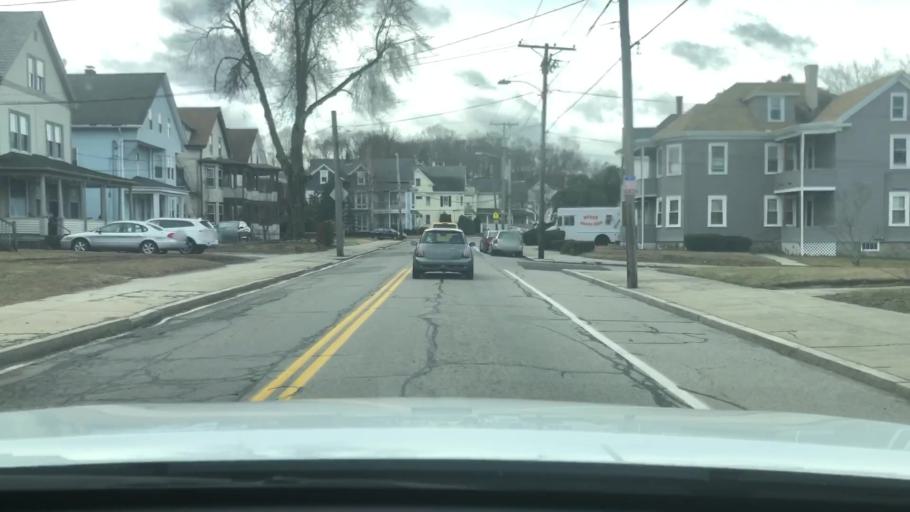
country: US
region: Rhode Island
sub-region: Providence County
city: Woonsocket
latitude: 41.9921
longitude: -71.5272
